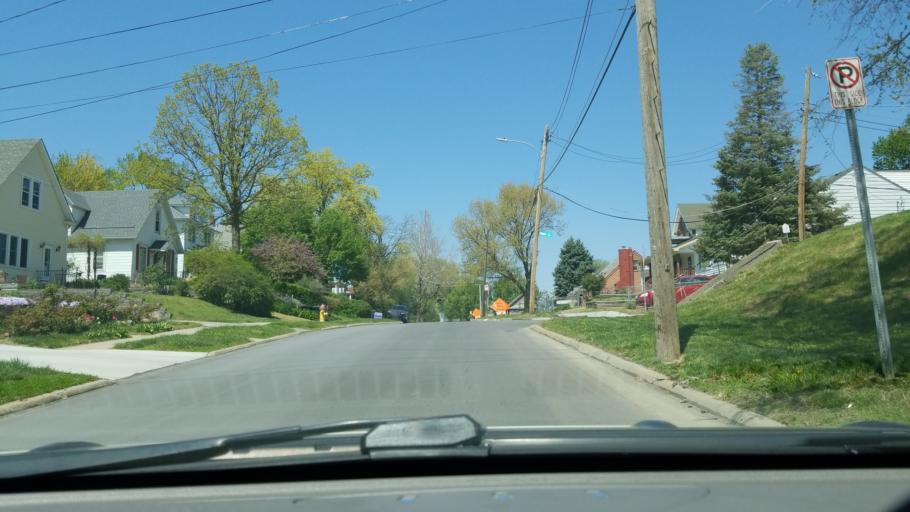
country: US
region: Nebraska
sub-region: Douglas County
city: Omaha
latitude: 41.2238
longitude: -95.9374
